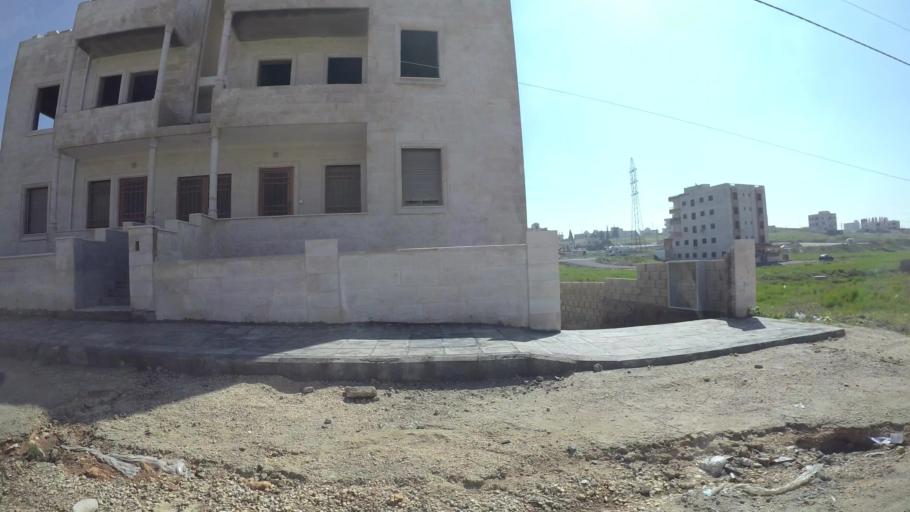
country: JO
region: Amman
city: Al Bunayyat ash Shamaliyah
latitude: 31.8909
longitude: 35.9016
